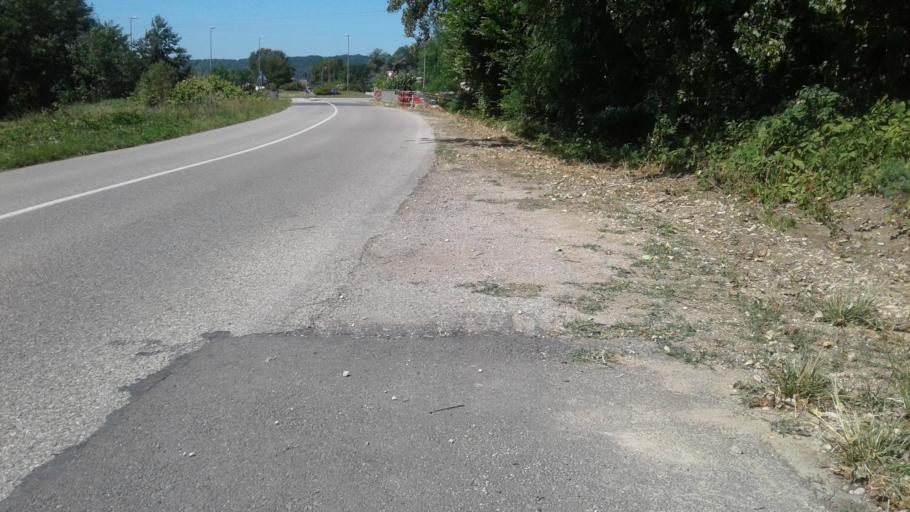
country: FR
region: Rhone-Alpes
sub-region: Departement de l'Ain
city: Beynost
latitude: 45.8279
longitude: 5.0116
